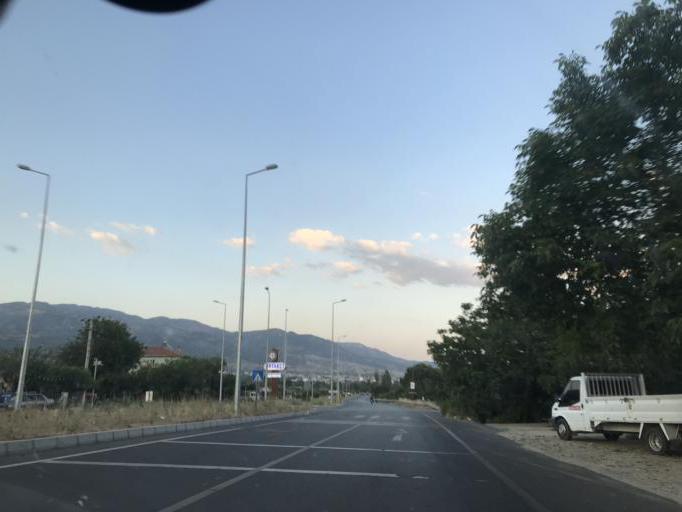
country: TR
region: Aydin
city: Buharkent
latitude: 37.9579
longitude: 28.7121
